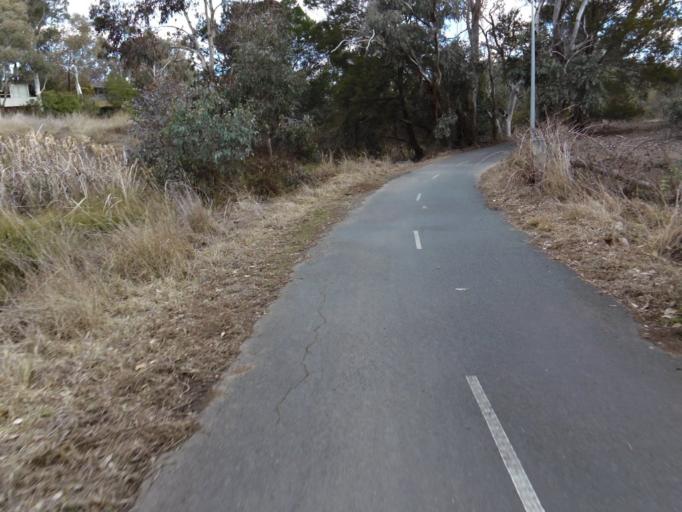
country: AU
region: Australian Capital Territory
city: Acton
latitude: -35.2558
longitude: 149.1101
